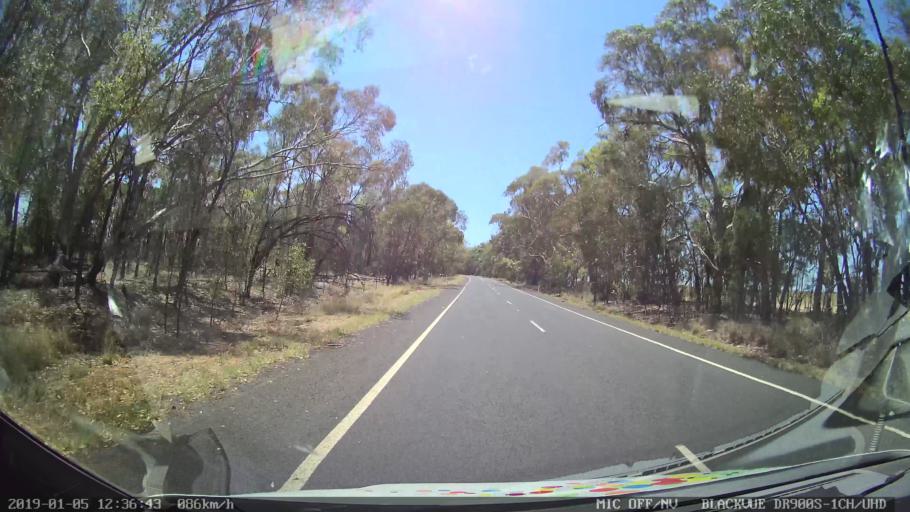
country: AU
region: New South Wales
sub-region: Warrumbungle Shire
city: Coonabarabran
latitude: -31.2065
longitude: 149.4445
